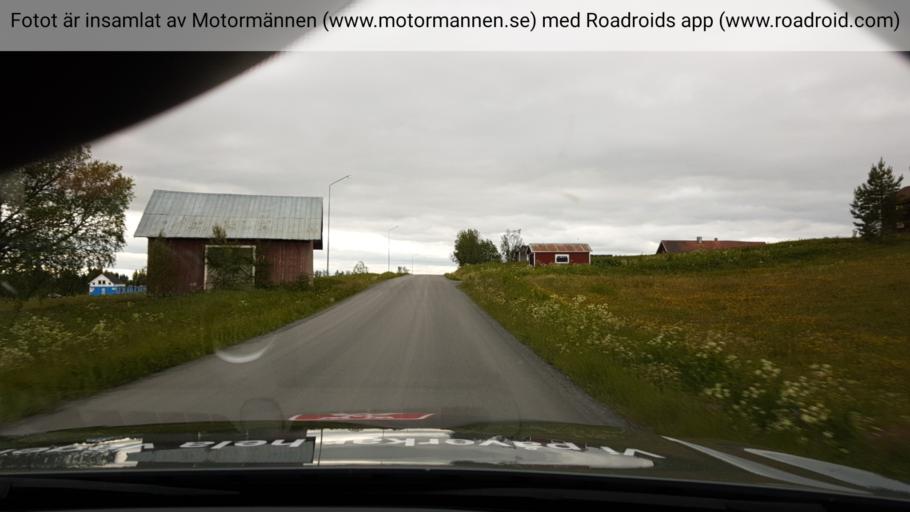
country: SE
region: Jaemtland
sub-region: OEstersunds Kommun
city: Lit
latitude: 63.5654
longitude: 14.9227
